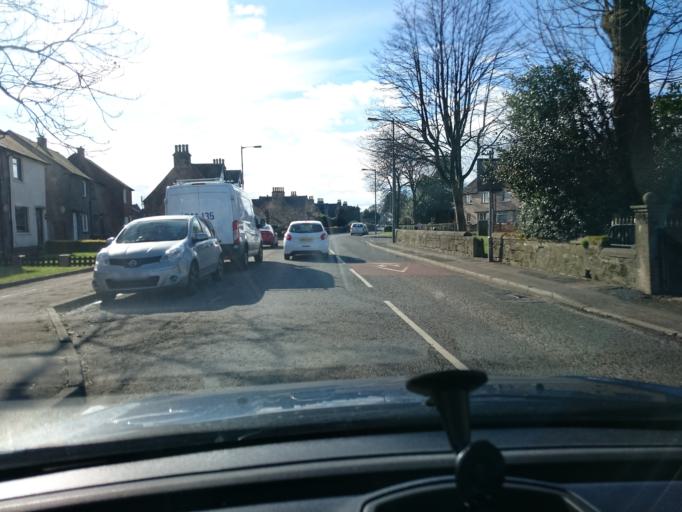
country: GB
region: Scotland
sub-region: Falkirk
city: Bonnybridge
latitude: 56.0041
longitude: -3.8907
